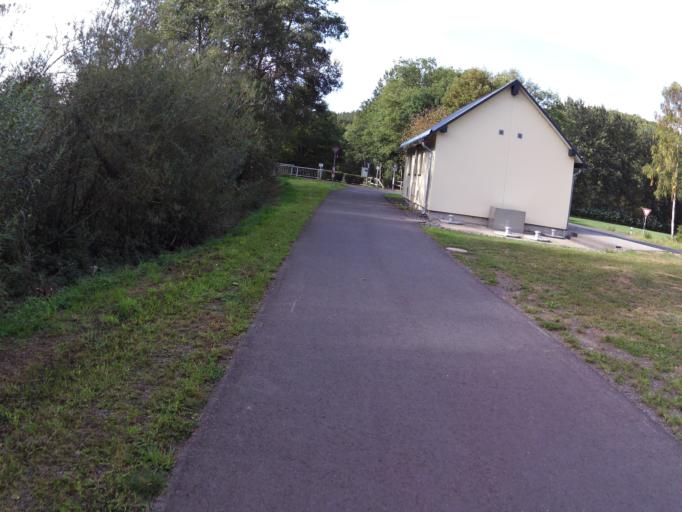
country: DE
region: Rheinland-Pfalz
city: Winterspelt
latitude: 50.2365
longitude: 6.1976
